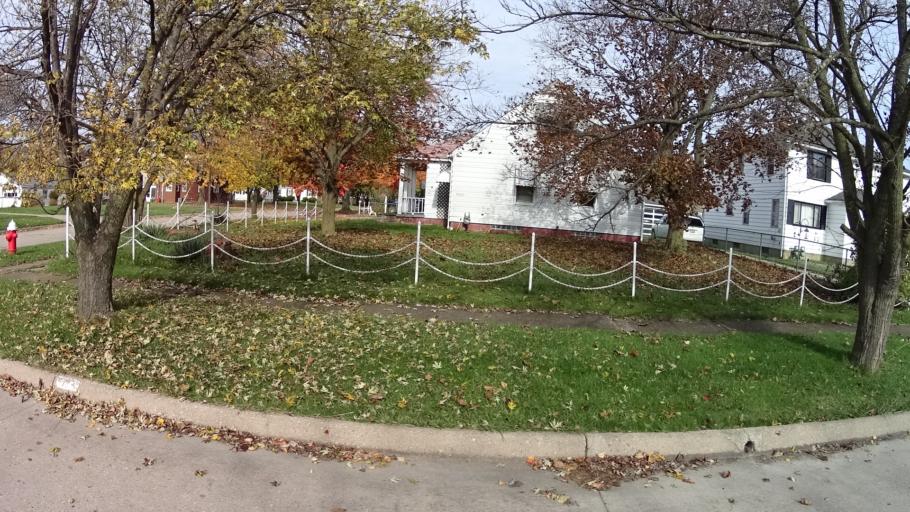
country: US
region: Ohio
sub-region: Lorain County
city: Sheffield Lake
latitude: 41.4723
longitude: -82.1343
